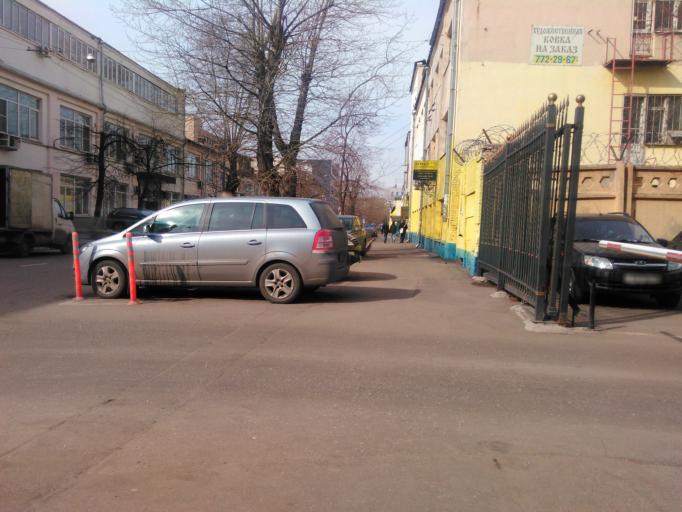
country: RU
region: Moscow
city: Mar'ina Roshcha
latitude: 55.8010
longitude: 37.5854
